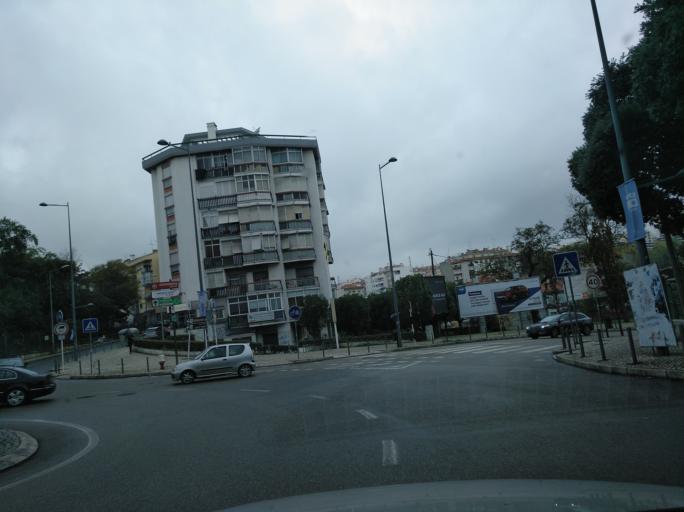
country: PT
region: Lisbon
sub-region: Loures
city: Sacavem
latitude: 38.7941
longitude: -9.1039
